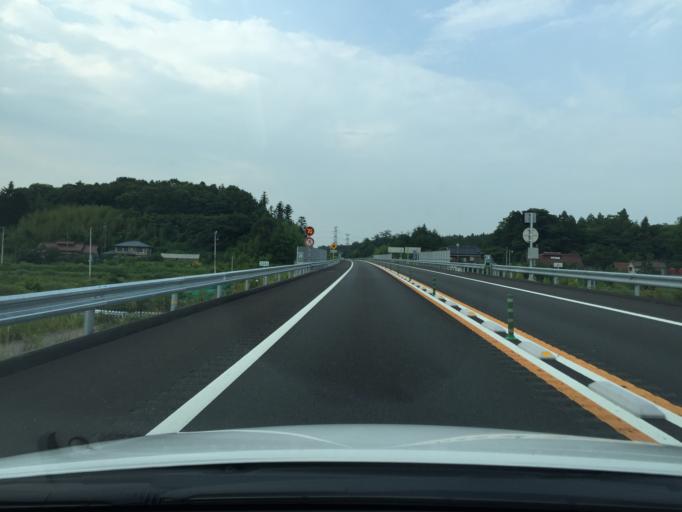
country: JP
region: Fukushima
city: Namie
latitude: 37.5169
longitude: 140.9441
